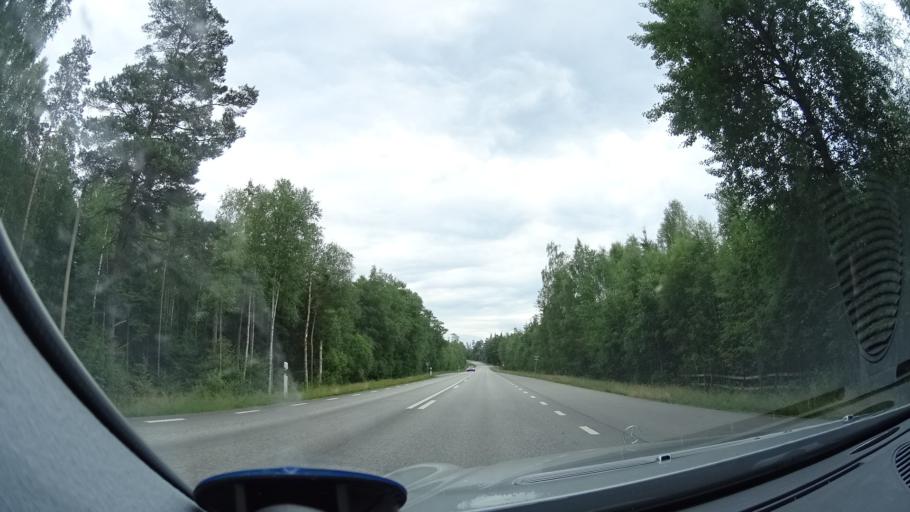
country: SE
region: Kronoberg
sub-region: Tingsryds Kommun
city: Tingsryd
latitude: 56.4998
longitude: 14.9957
